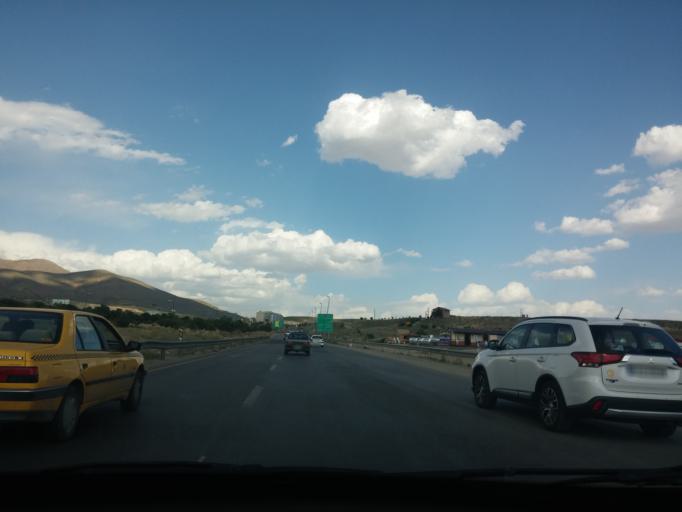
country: IR
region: Tehran
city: Damavand
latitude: 35.7189
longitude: 51.9211
